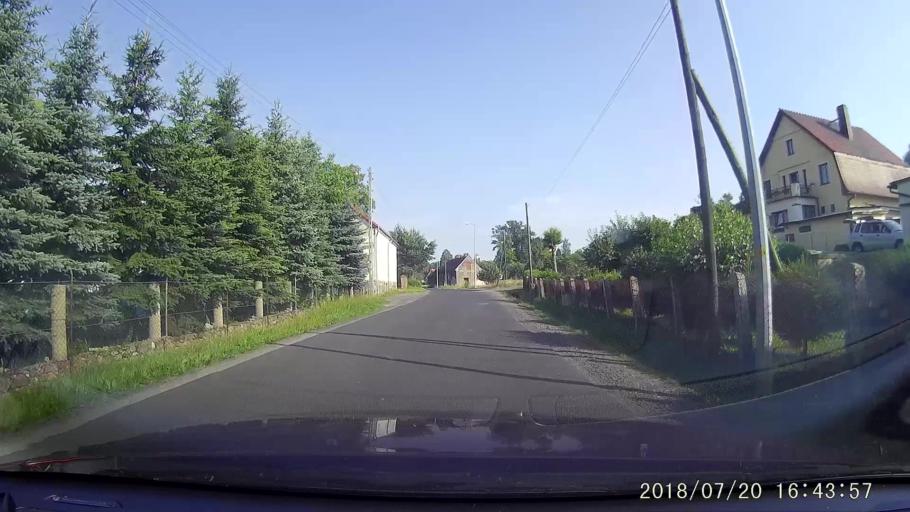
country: PL
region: Lower Silesian Voivodeship
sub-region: Powiat lubanski
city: Siekierczyn
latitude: 51.0706
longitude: 15.1635
